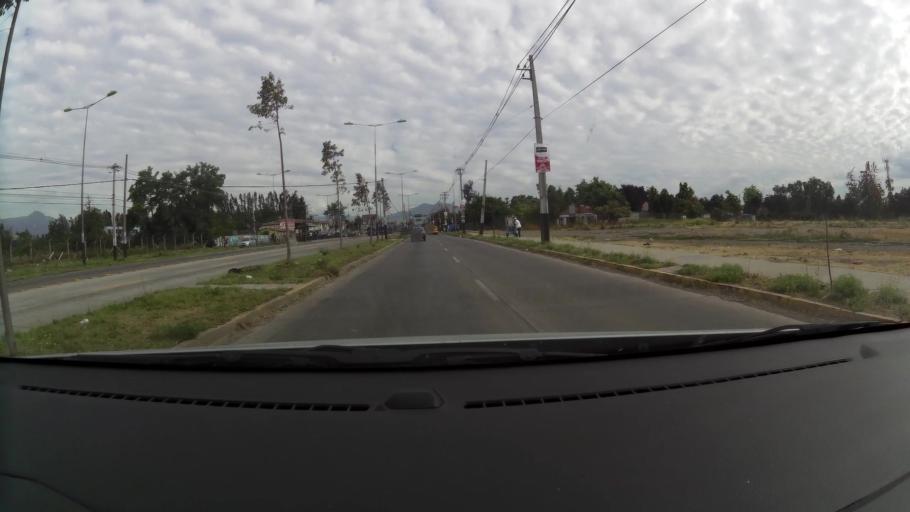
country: CL
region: Santiago Metropolitan
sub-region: Provincia de Santiago
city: La Pintana
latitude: -33.5819
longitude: -70.6292
